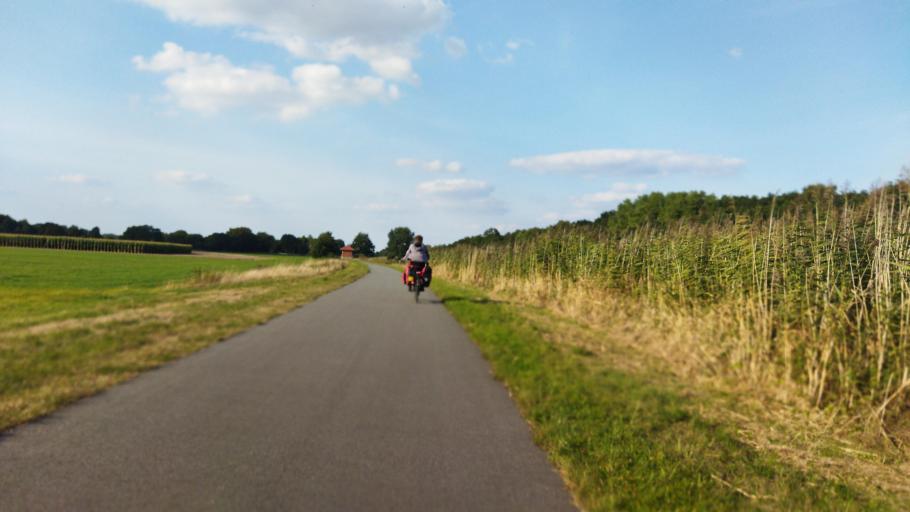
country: DE
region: Lower Saxony
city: Lehe
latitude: 53.0192
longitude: 7.3217
